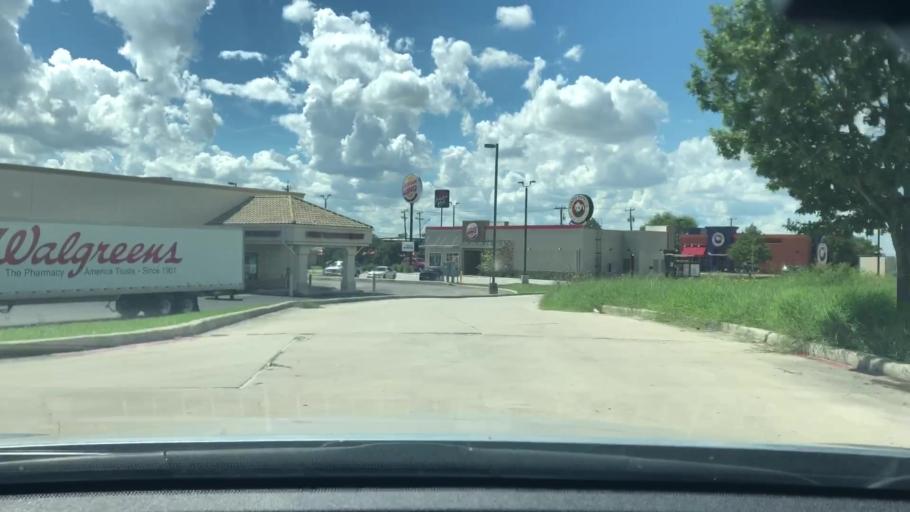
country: US
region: Texas
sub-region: Bexar County
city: Kirby
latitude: 29.4814
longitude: -98.3608
